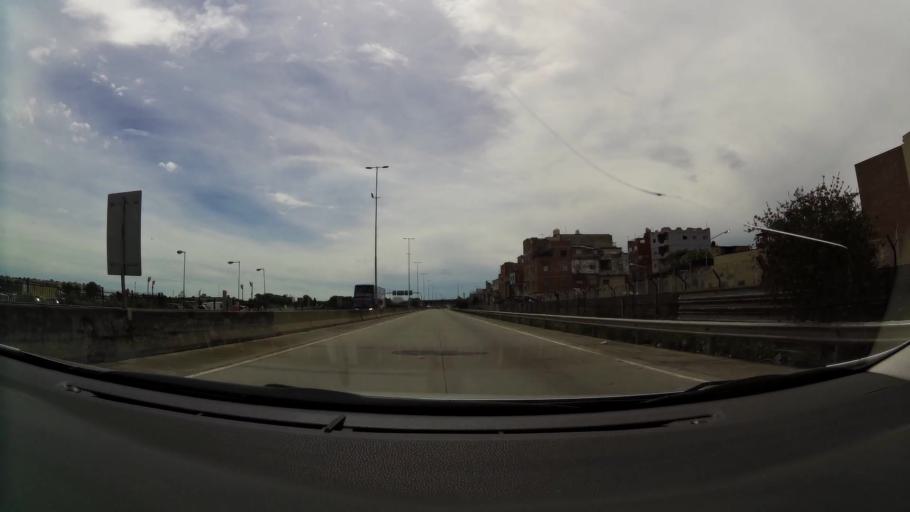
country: AR
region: Buenos Aires F.D.
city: Villa Lugano
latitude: -34.6591
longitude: -58.4574
